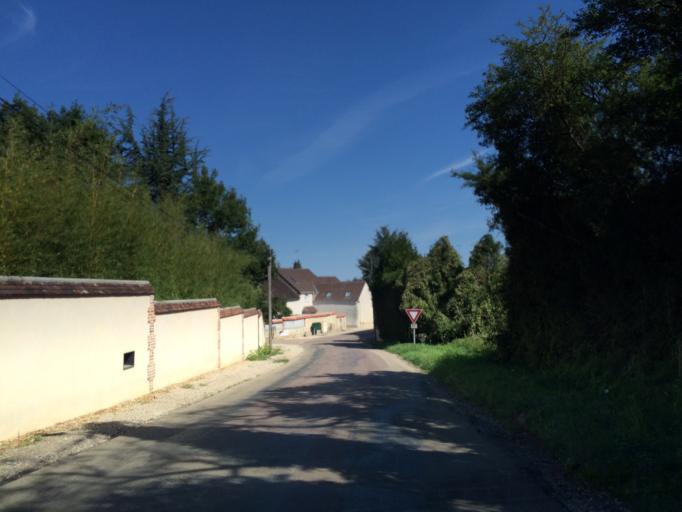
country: FR
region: Bourgogne
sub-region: Departement de l'Yonne
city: Aillant-sur-Tholon
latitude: 47.8423
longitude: 3.3930
